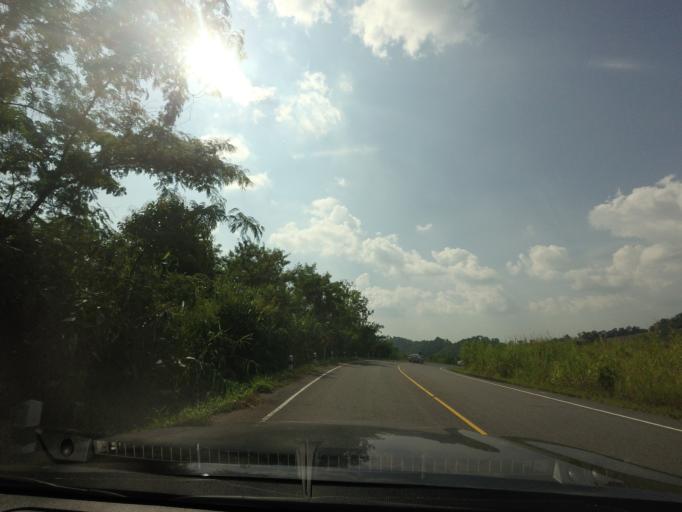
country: TH
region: Nan
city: Santi Suk
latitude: 18.9787
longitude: 101.0040
